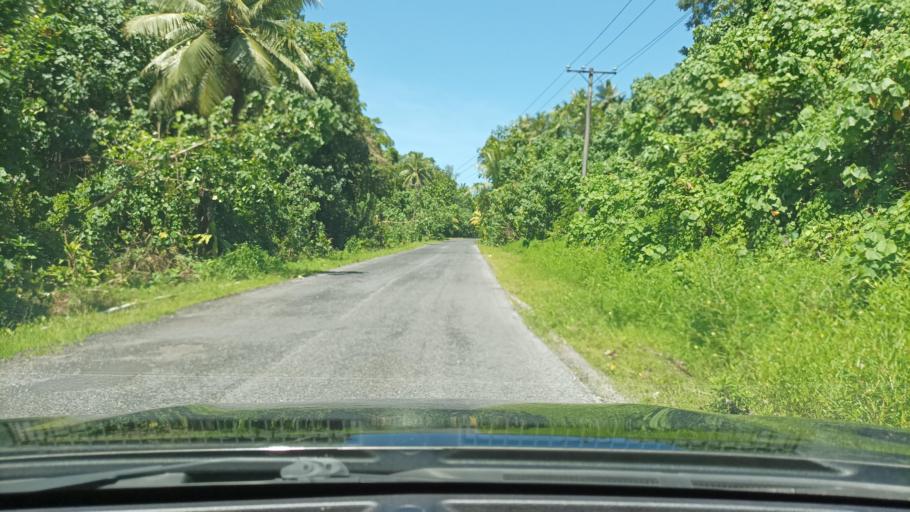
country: FM
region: Pohnpei
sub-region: Madolenihm Municipality
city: Madolenihm Municipality Government
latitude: 6.9206
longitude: 158.3163
